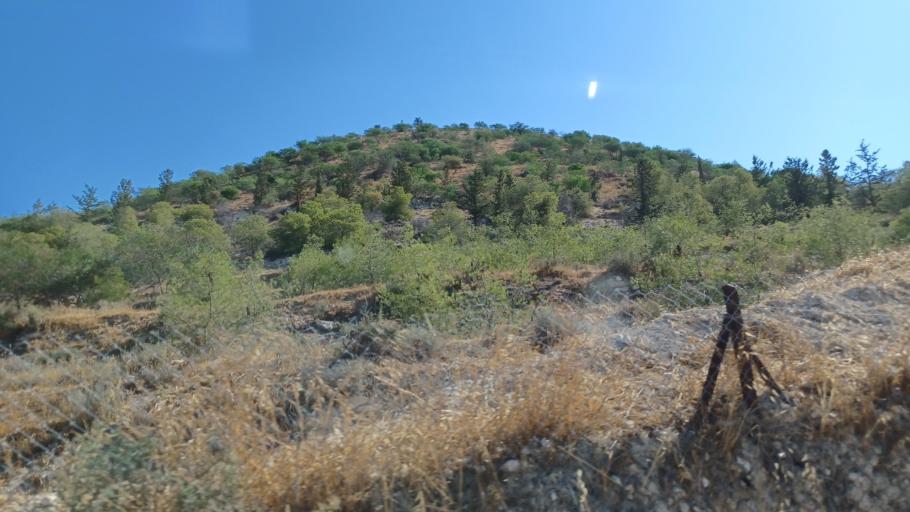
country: CY
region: Lefkosia
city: Lympia
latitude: 34.9778
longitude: 33.4982
